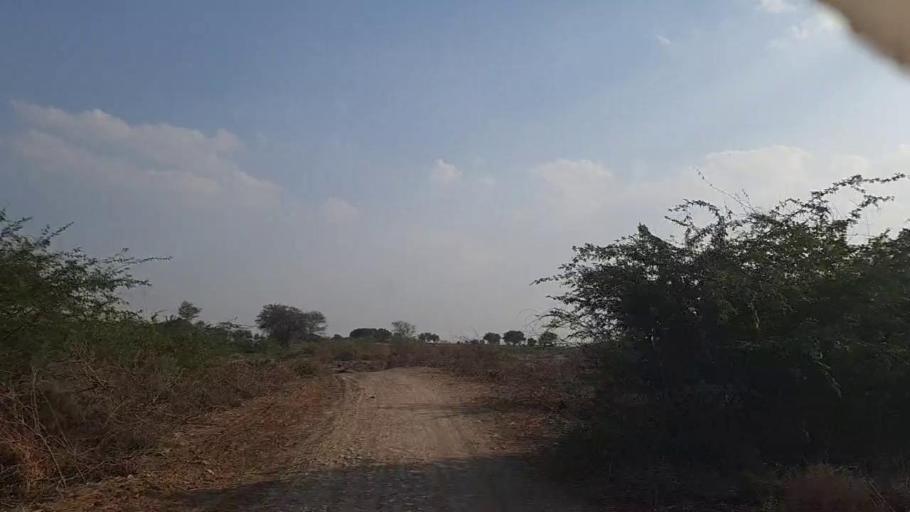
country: PK
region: Sindh
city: Jati
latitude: 24.4283
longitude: 68.3761
